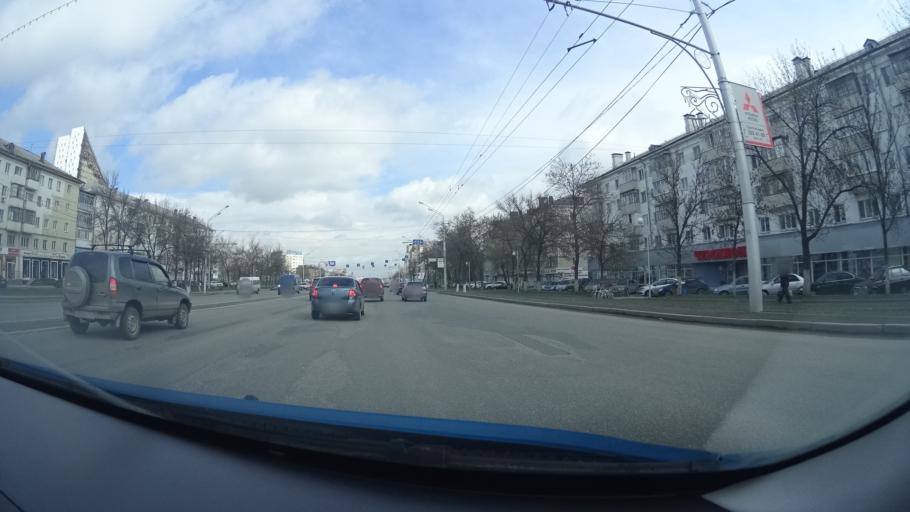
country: RU
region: Bashkortostan
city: Ufa
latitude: 54.7804
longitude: 56.0319
